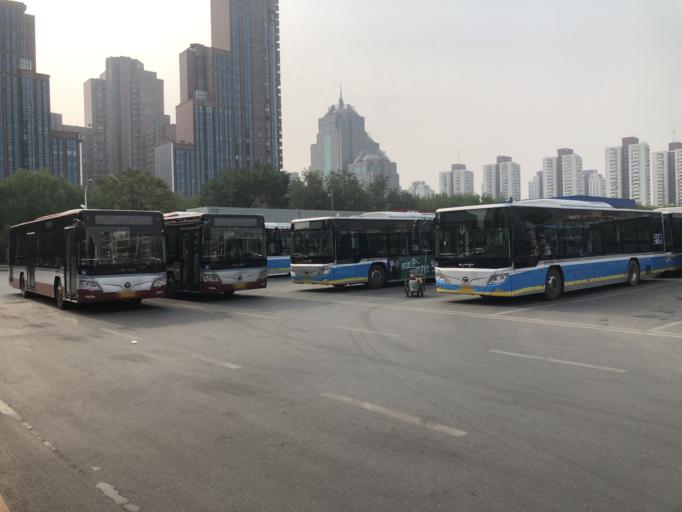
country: CN
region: Beijing
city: Datun
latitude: 39.9970
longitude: 116.4004
